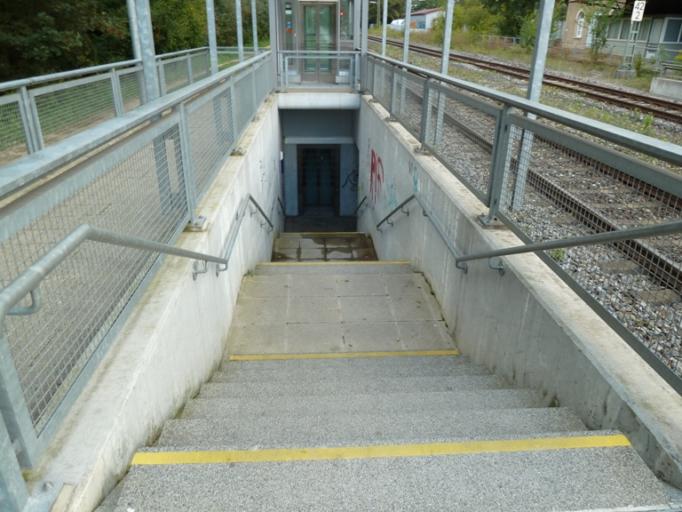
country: DE
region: Baden-Wuerttemberg
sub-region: Tuebingen Region
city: Kirchentellinsfurt
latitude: 48.5293
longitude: 9.1386
